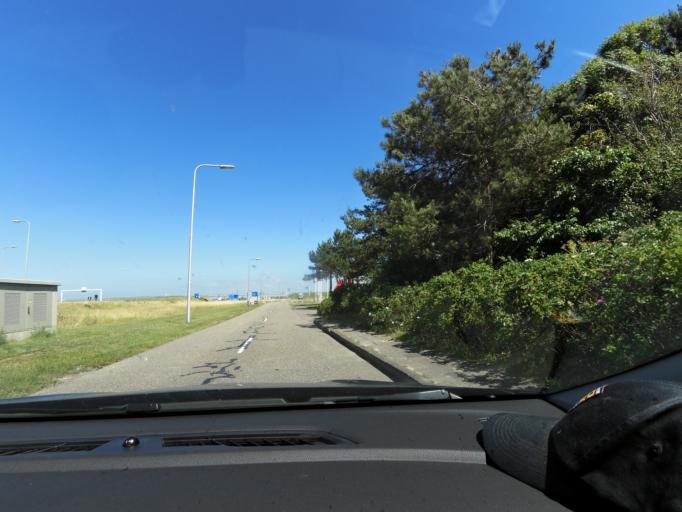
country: NL
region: Friesland
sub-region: Sudwest Fryslan
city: Makkum
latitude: 53.0737
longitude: 5.3370
